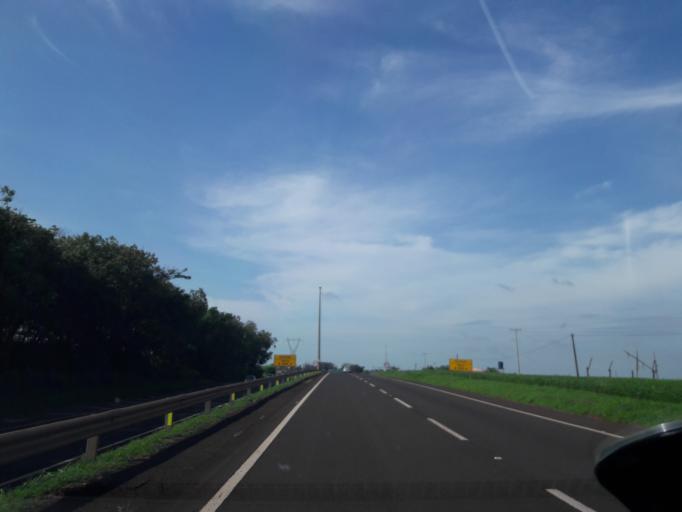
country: BR
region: Parana
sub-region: Paicandu
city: Paicandu
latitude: -23.5993
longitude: -52.0798
